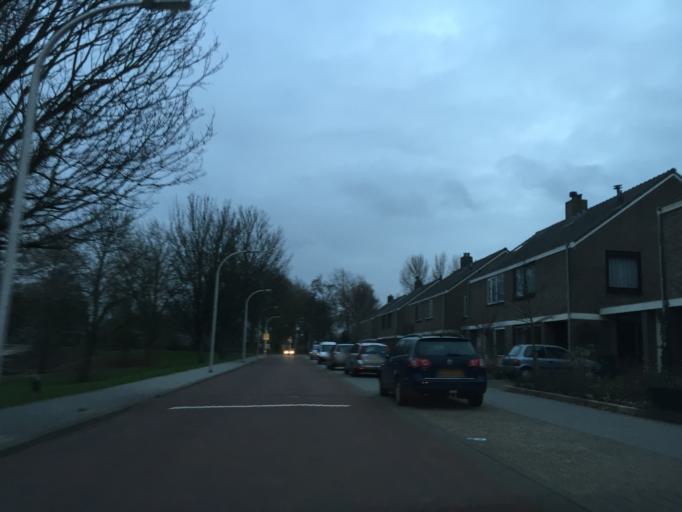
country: NL
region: South Holland
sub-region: Gemeente Pijnacker-Nootdorp
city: Pijnacker
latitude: 52.0253
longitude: 4.4272
